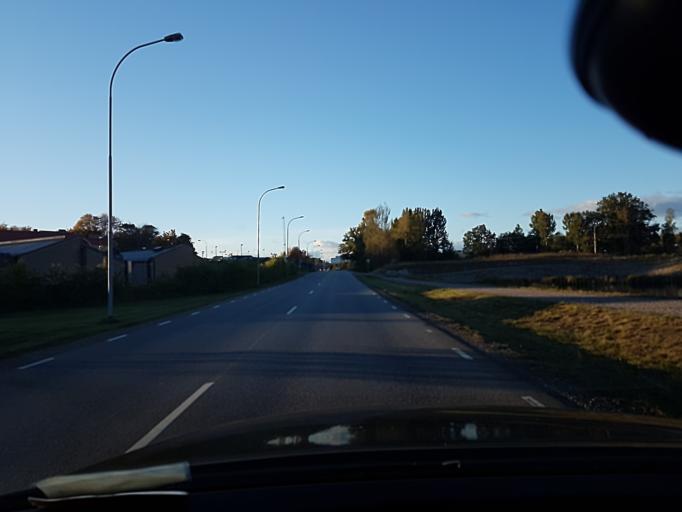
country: SE
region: Kronoberg
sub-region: Vaxjo Kommun
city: Vaexjoe
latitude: 56.8678
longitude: 14.8307
